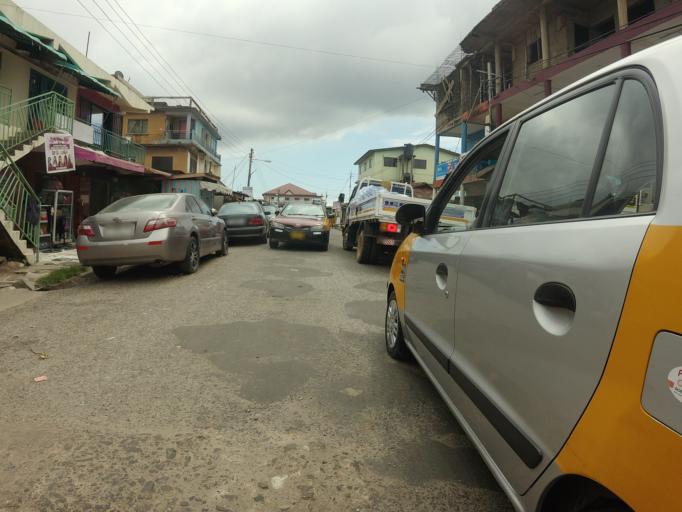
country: GH
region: Greater Accra
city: Accra
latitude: 5.5833
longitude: -0.2076
